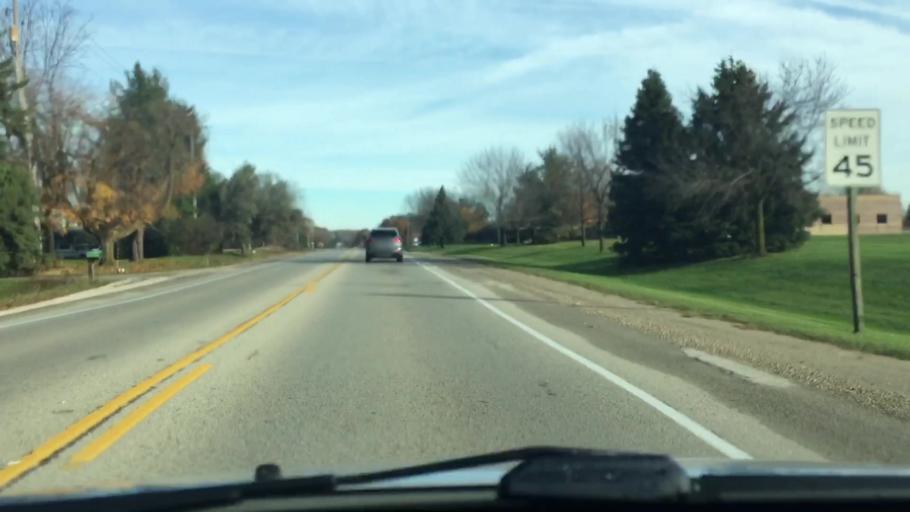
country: US
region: Wisconsin
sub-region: Waukesha County
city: Hartland
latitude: 43.0820
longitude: -88.3632
